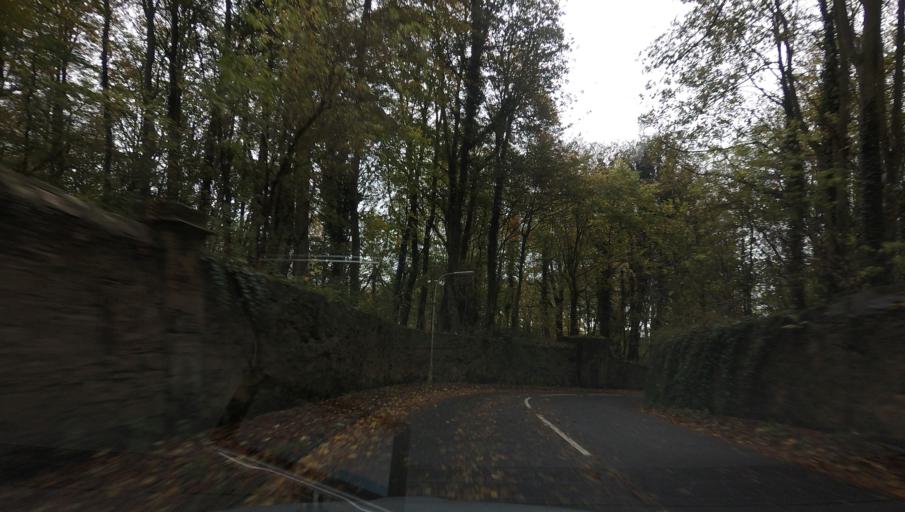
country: GB
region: Scotland
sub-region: Fife
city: East Wemyss
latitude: 56.1414
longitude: -3.0895
